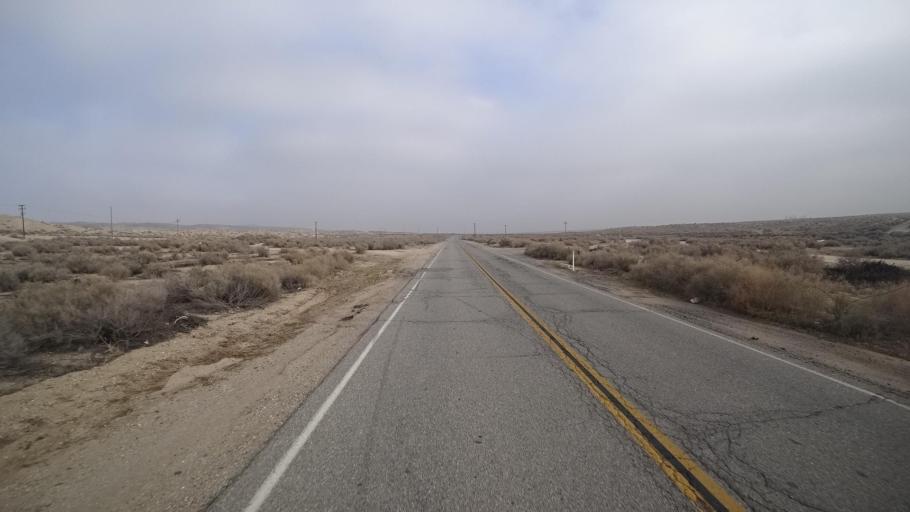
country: US
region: California
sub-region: Kern County
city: South Taft
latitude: 35.1368
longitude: -119.4122
